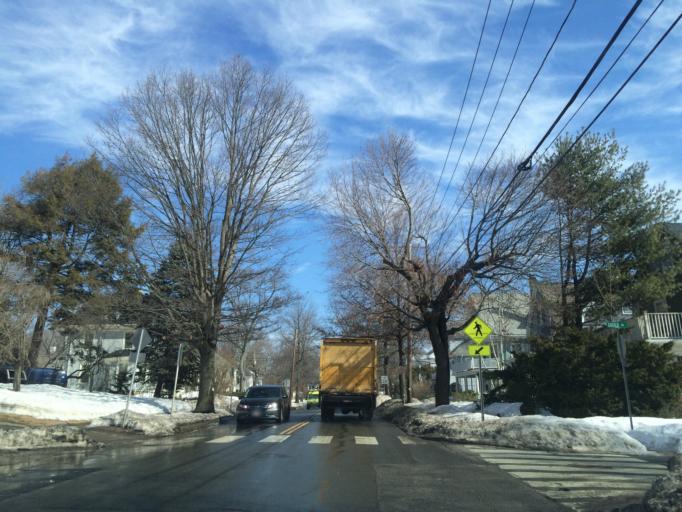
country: US
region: Massachusetts
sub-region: Middlesex County
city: Arlington
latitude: 42.4089
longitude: -71.1594
